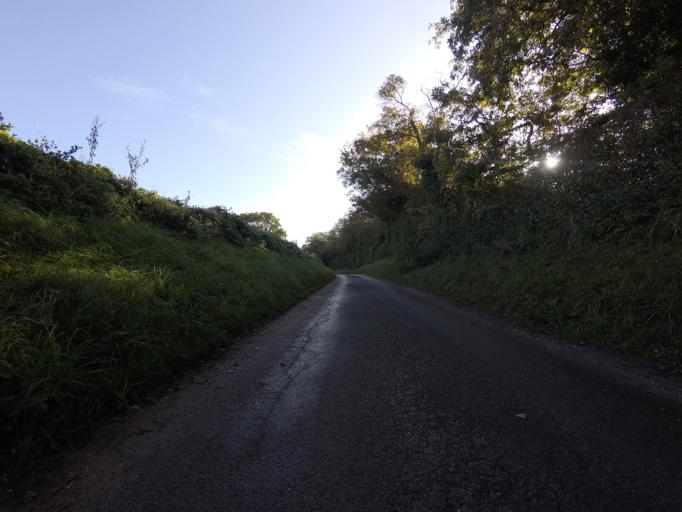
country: GB
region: England
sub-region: Norfolk
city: Dersingham
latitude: 52.8210
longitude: 0.5288
